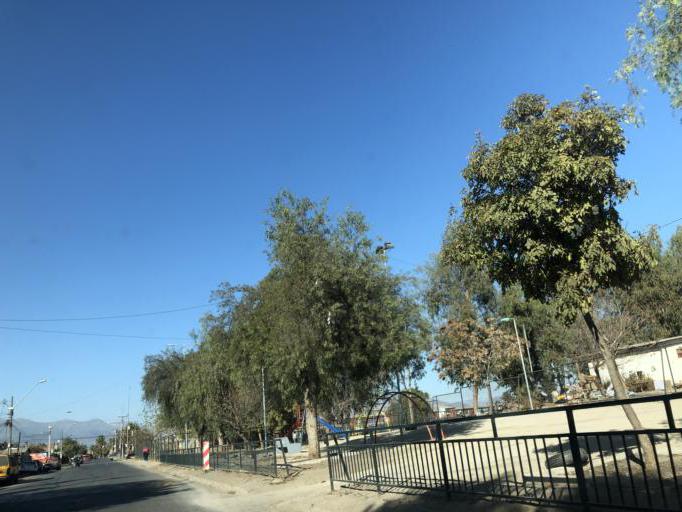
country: CL
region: Santiago Metropolitan
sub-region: Provincia de Cordillera
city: Puente Alto
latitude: -33.6182
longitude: -70.5953
